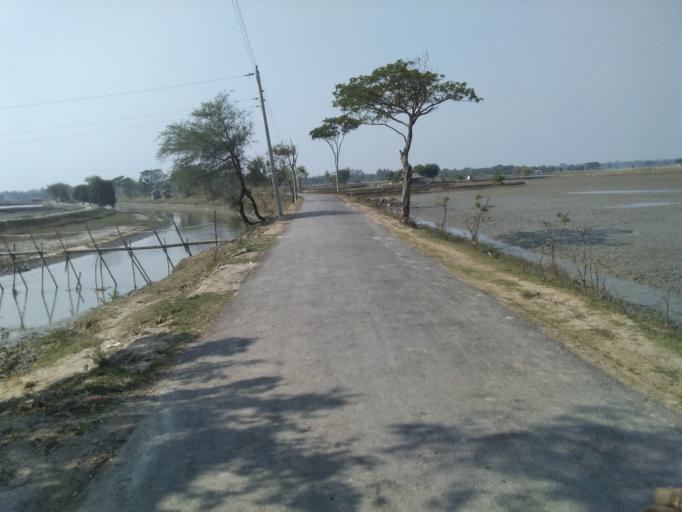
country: IN
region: West Bengal
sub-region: North 24 Parganas
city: Taki
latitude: 22.6350
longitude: 89.0084
